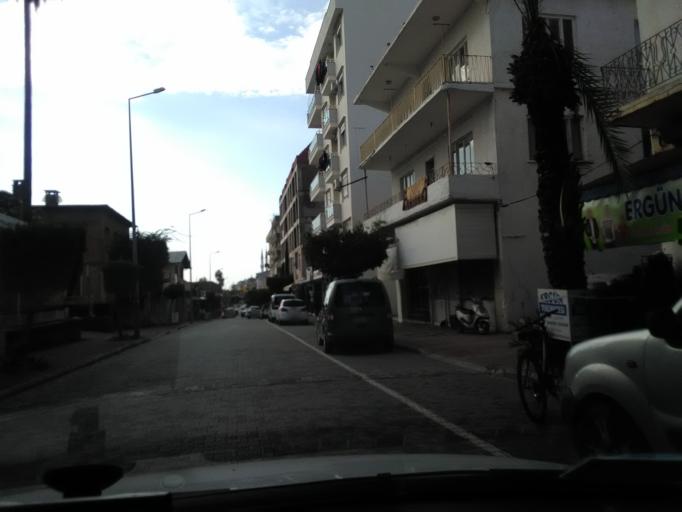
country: TR
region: Antalya
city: Gazipasa
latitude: 36.2687
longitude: 32.3199
